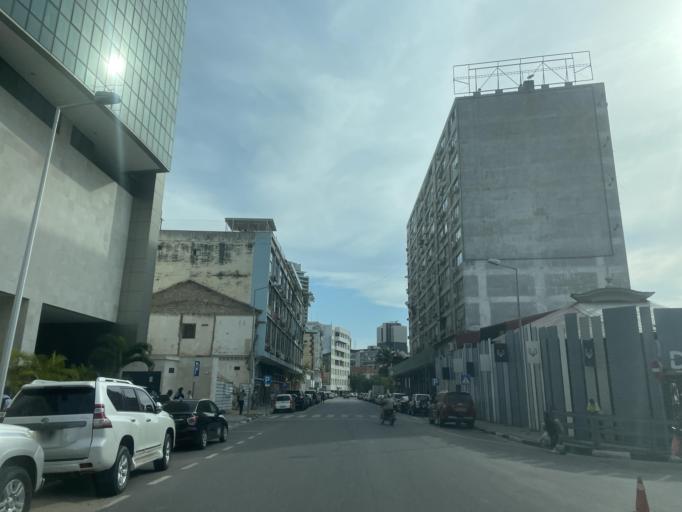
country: AO
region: Luanda
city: Luanda
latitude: -8.8111
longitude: 13.2370
